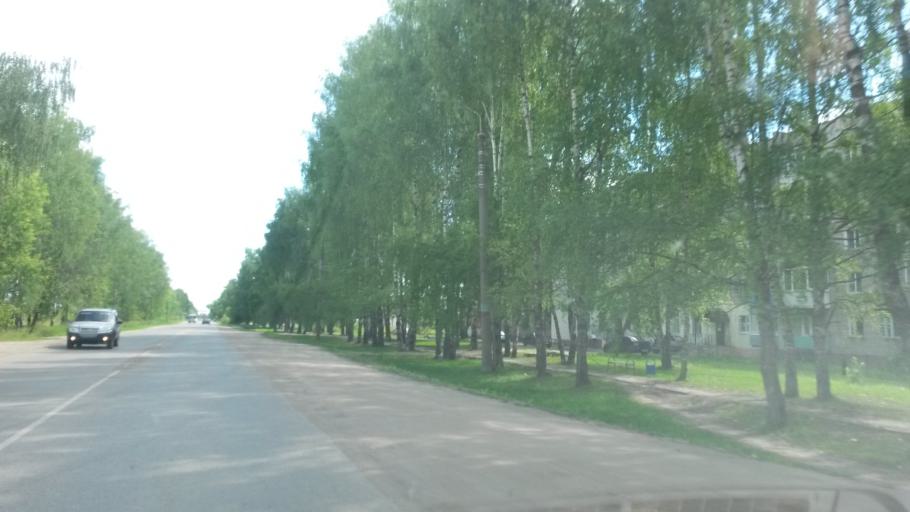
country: RU
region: Ivanovo
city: Zavolzhsk
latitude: 57.4782
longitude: 42.1512
